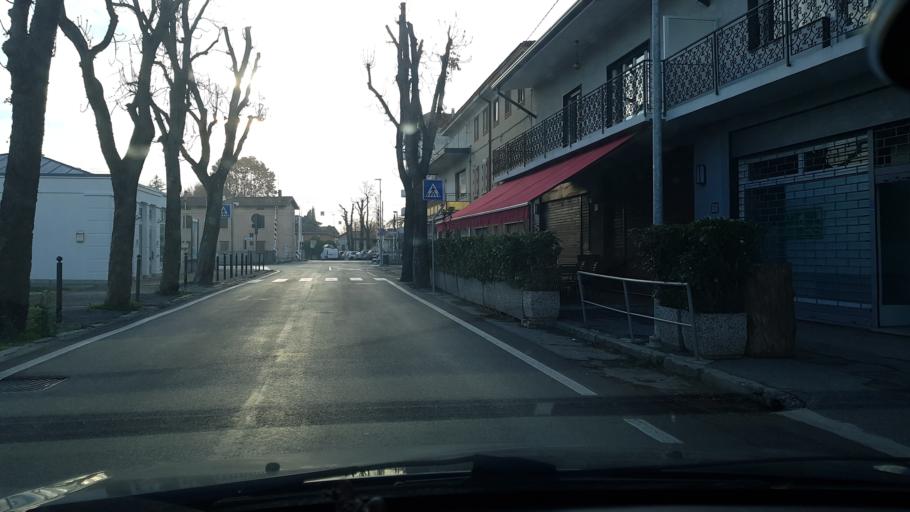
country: IT
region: Friuli Venezia Giulia
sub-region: Provincia di Gorizia
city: Ronchi dei Legionari
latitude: 45.8319
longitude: 13.5058
